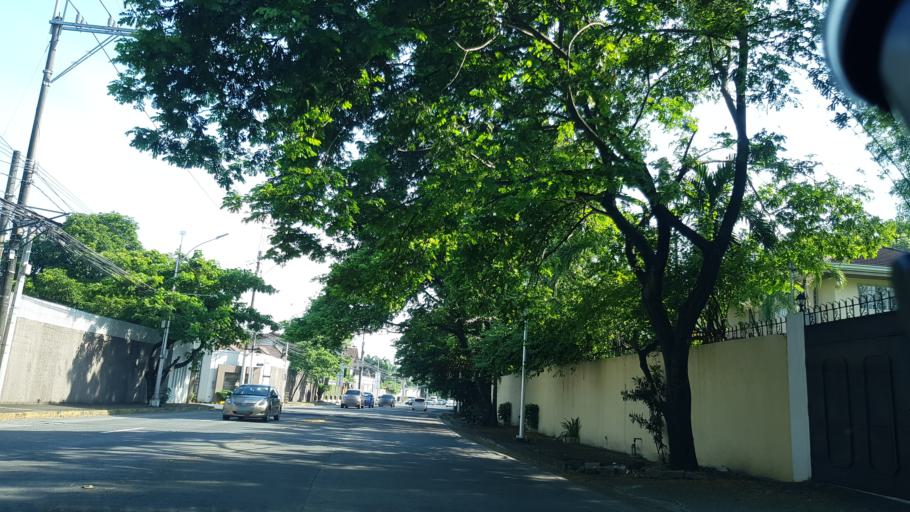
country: PH
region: Metro Manila
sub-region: Pasig
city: Pasig City
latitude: 14.5966
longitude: 121.0725
